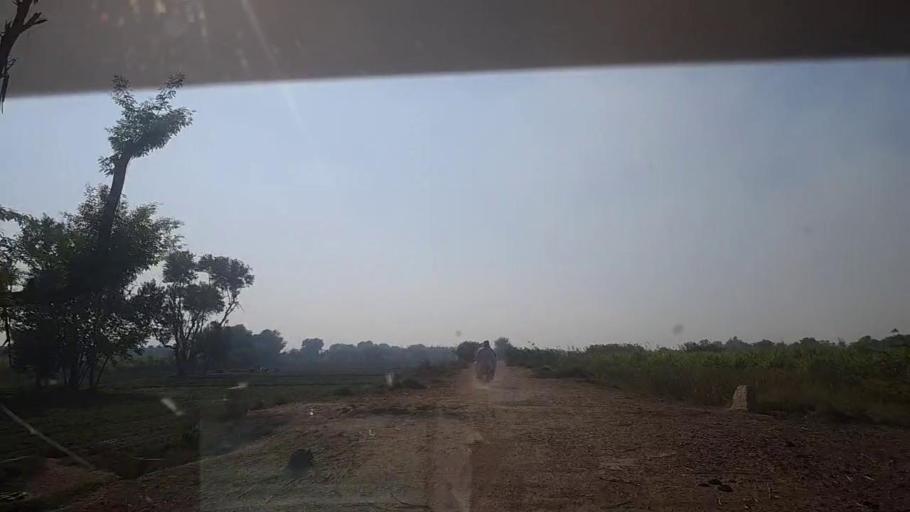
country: PK
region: Sindh
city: Gambat
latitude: 27.3738
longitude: 68.5718
